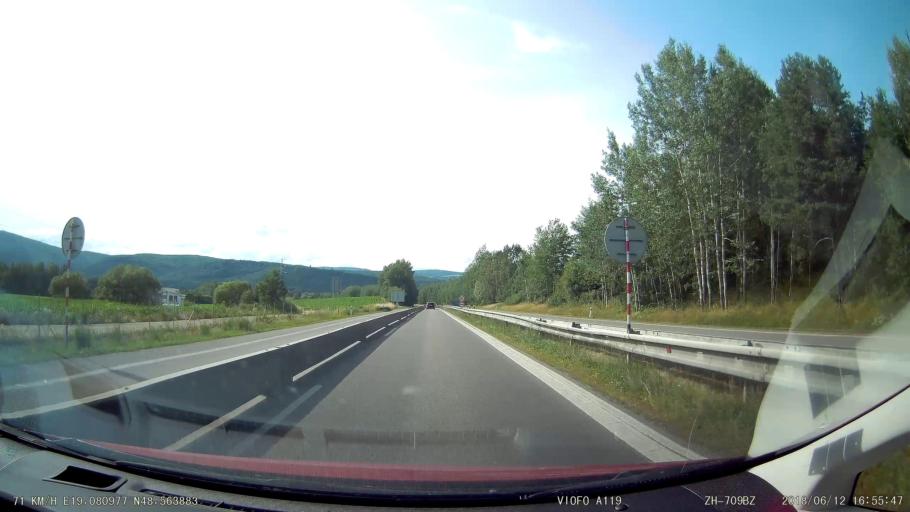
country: SK
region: Banskobystricky
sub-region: Okres Banska Bystrica
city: Zvolen
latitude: 48.5640
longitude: 19.0807
